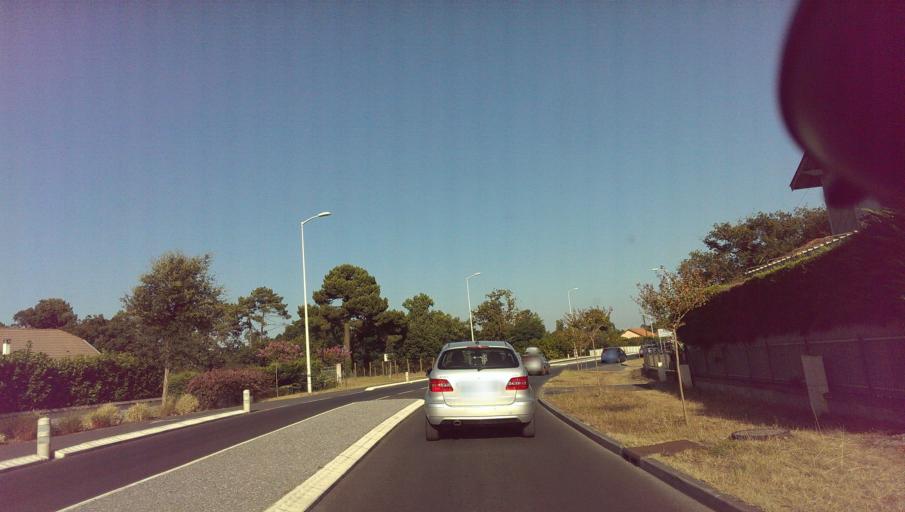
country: FR
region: Aquitaine
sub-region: Departement des Landes
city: Mimizan
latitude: 44.2099
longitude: -1.2492
